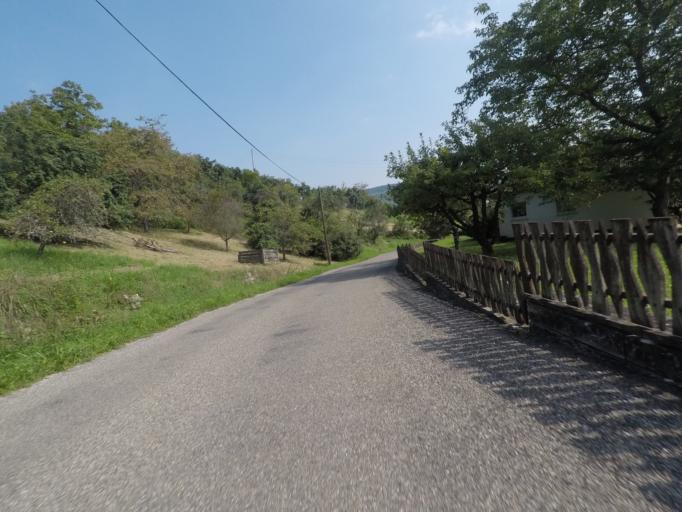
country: DE
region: Baden-Wuerttemberg
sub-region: Regierungsbezirk Stuttgart
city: Winterbach
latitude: 48.8036
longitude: 9.4308
